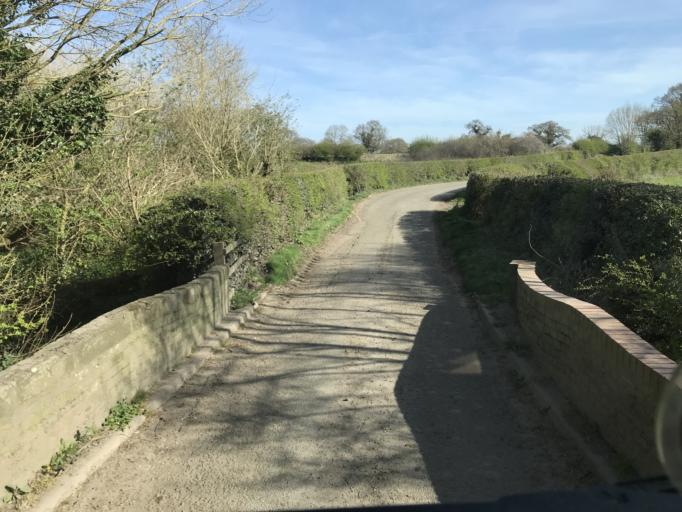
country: GB
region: England
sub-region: Cheshire West and Chester
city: Marston
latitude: 53.2273
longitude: -2.4756
